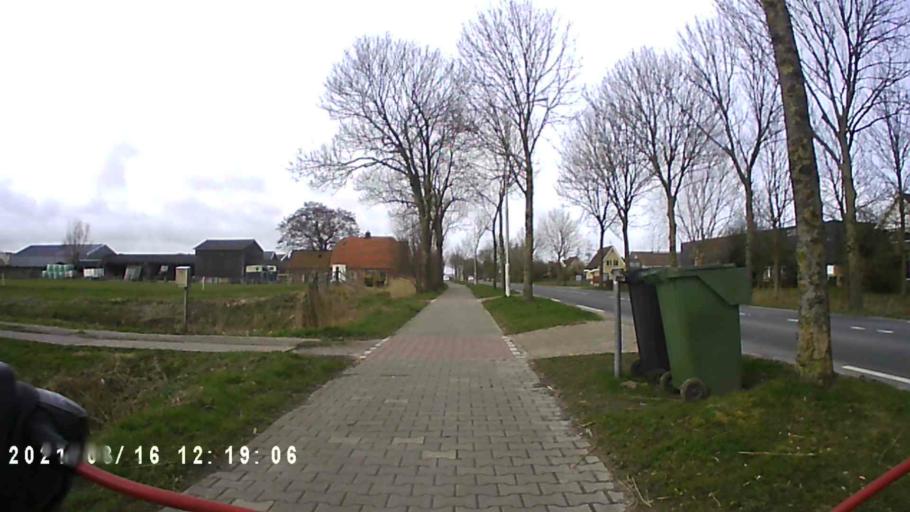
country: NL
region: Friesland
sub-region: Gemeente Ferwerderadiel
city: Hallum
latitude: 53.3079
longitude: 5.7741
